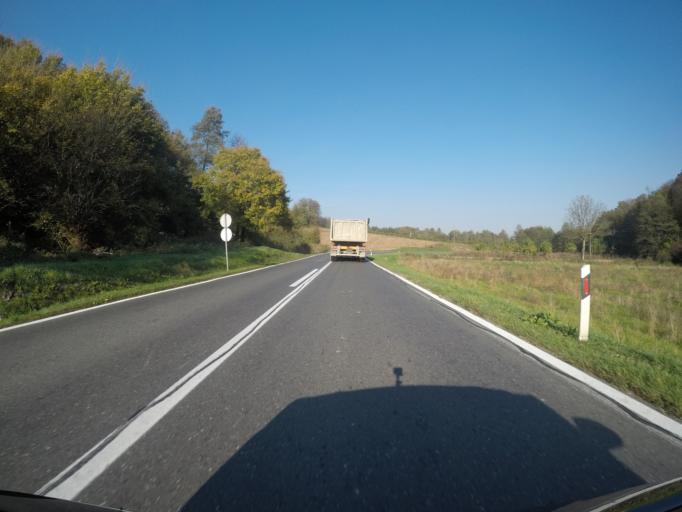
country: HR
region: Koprivnicko-Krizevacka
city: Virje
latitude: 46.0096
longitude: 16.9281
